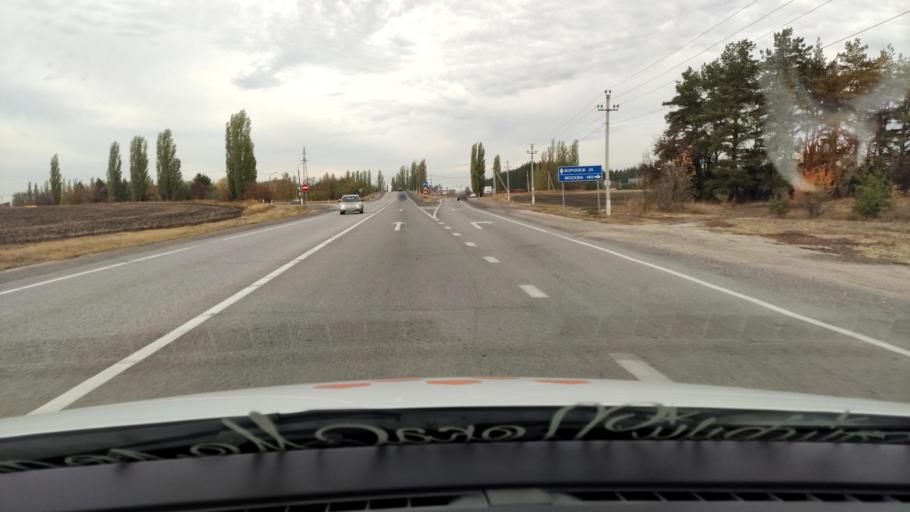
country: RU
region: Voronezj
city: Ramon'
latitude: 51.9296
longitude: 39.2268
